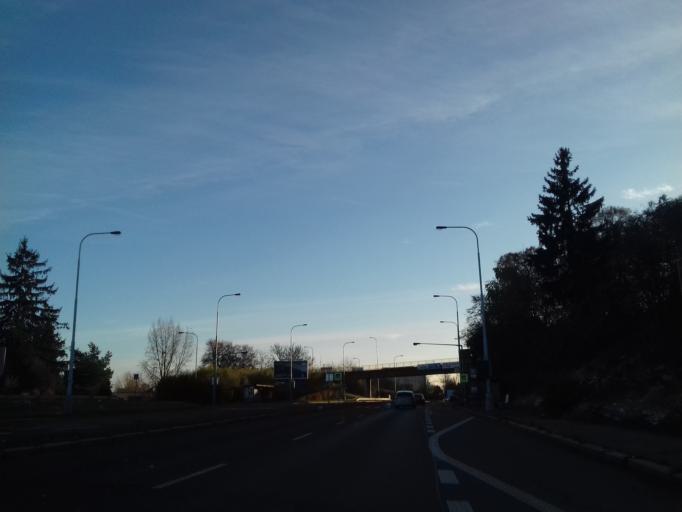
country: CZ
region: Central Bohemia
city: Hostivice
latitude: 50.0515
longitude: 14.3094
